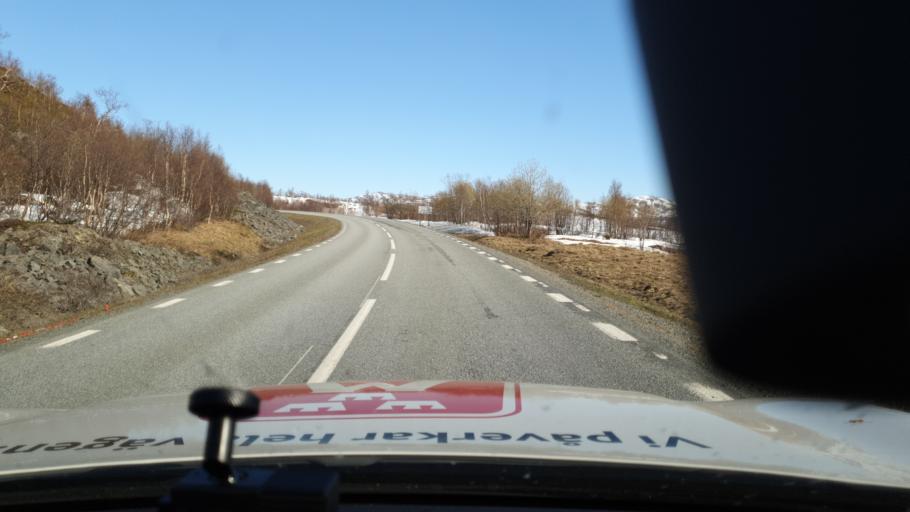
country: NO
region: Nordland
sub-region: Rana
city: Mo i Rana
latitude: 66.1269
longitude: 14.6035
